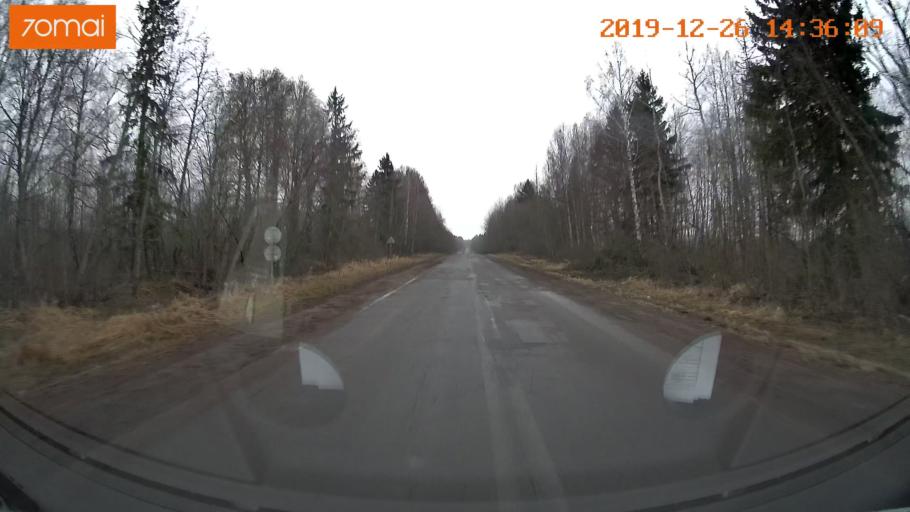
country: RU
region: Jaroslavl
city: Poshekhon'ye
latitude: 58.4141
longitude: 38.9772
